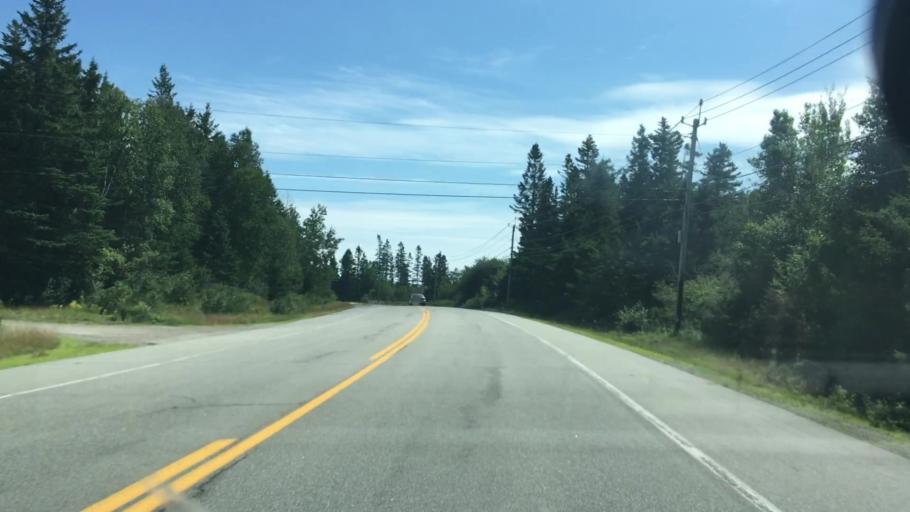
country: US
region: Maine
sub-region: Washington County
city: Eastport
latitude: 44.9431
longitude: -67.0388
